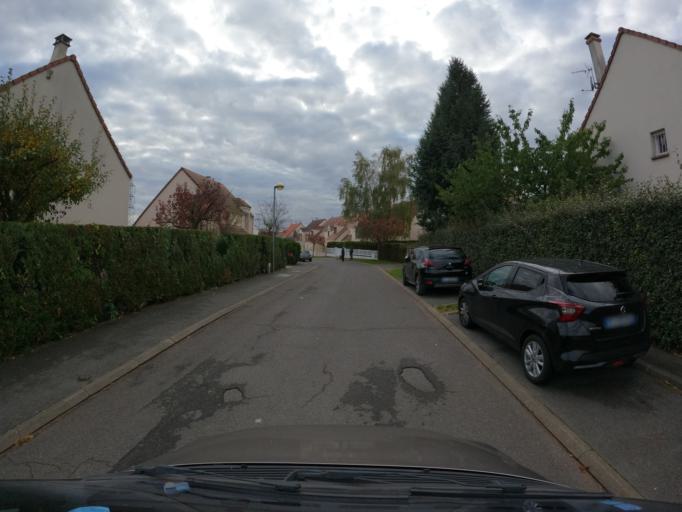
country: FR
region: Ile-de-France
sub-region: Departement de Seine-Saint-Denis
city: Montfermeil
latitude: 48.8878
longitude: 2.5787
